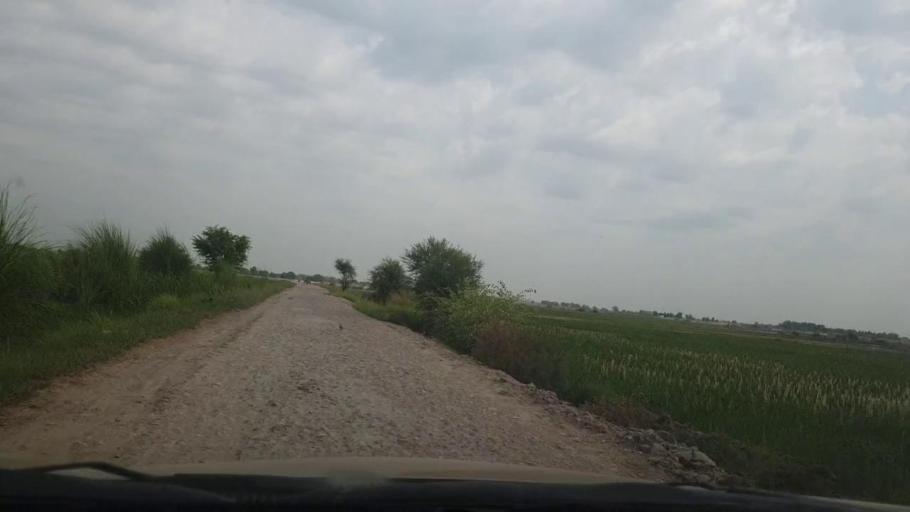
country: PK
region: Sindh
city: Ratodero
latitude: 27.7205
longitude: 68.2316
